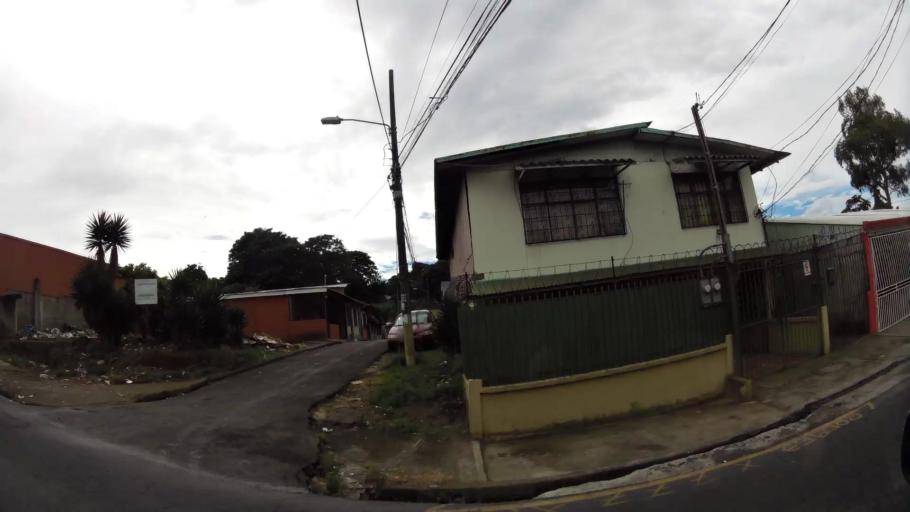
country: CR
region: San Jose
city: Purral
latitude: 9.9555
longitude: -84.0351
